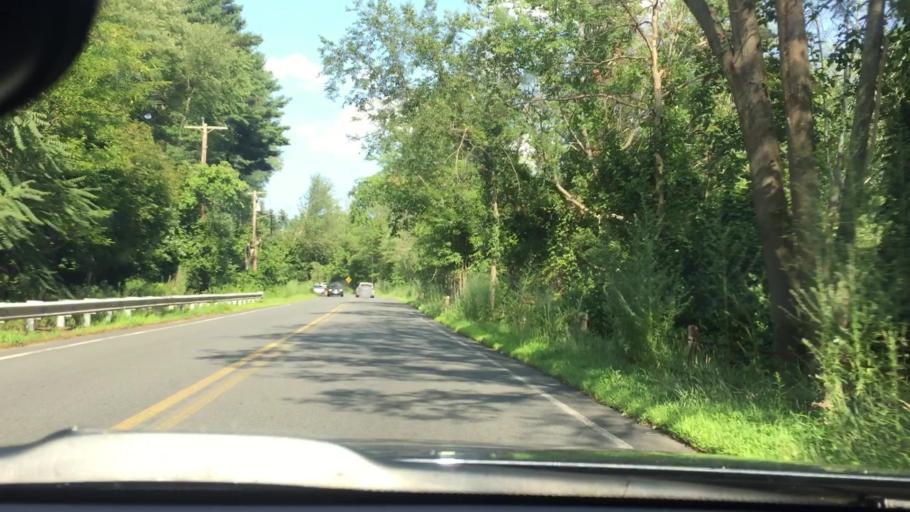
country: US
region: Massachusetts
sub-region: Norfolk County
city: Dedham
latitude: 42.2702
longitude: -71.1944
